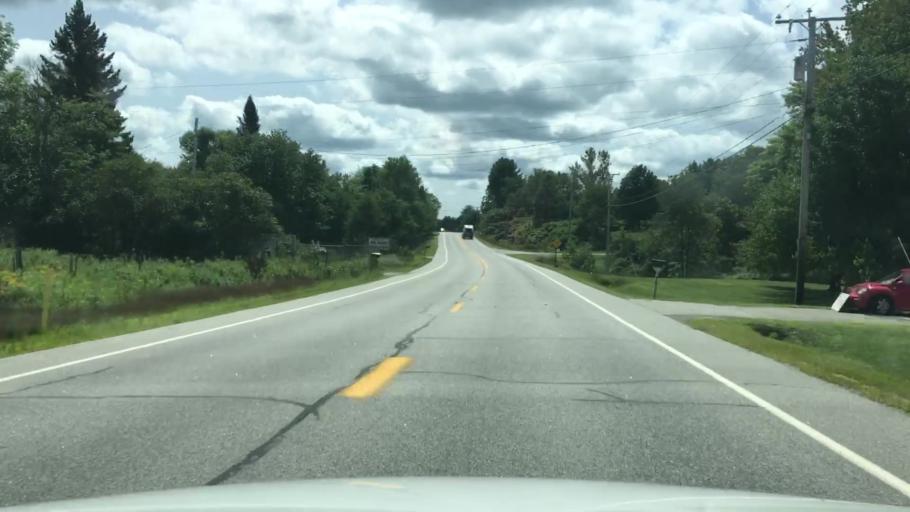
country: US
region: Maine
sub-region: Kennebec County
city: Pittston
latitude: 44.1641
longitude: -69.7450
